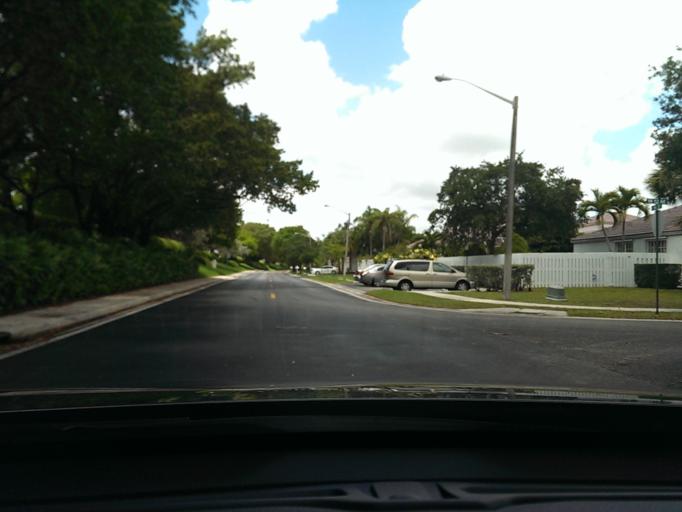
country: US
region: Florida
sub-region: Broward County
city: Sunshine Ranches
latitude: 26.0084
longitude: -80.3457
